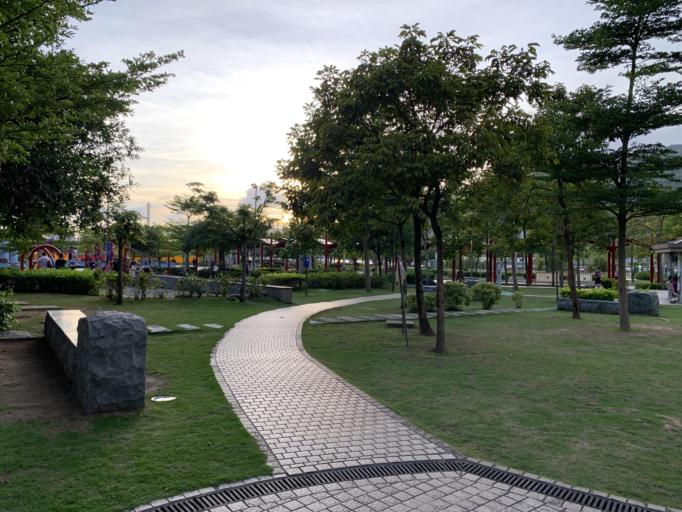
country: HK
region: Tsuen Wan
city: Tsuen Wan
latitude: 22.3626
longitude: 114.1002
